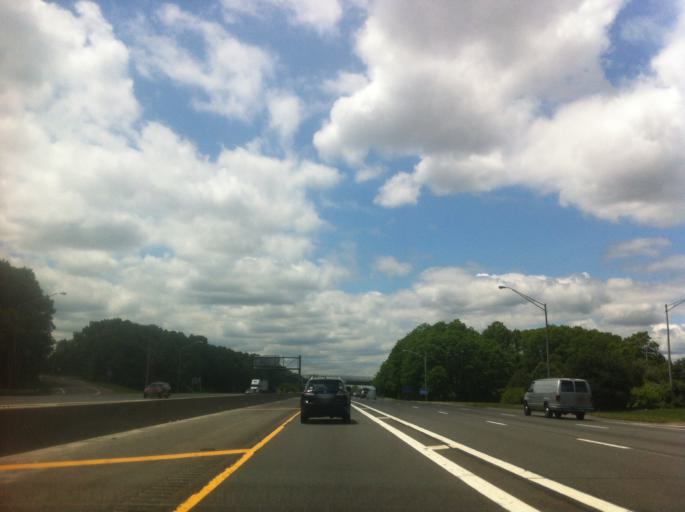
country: US
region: New York
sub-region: Suffolk County
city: Wheatley Heights
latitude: 40.7899
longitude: -73.3694
